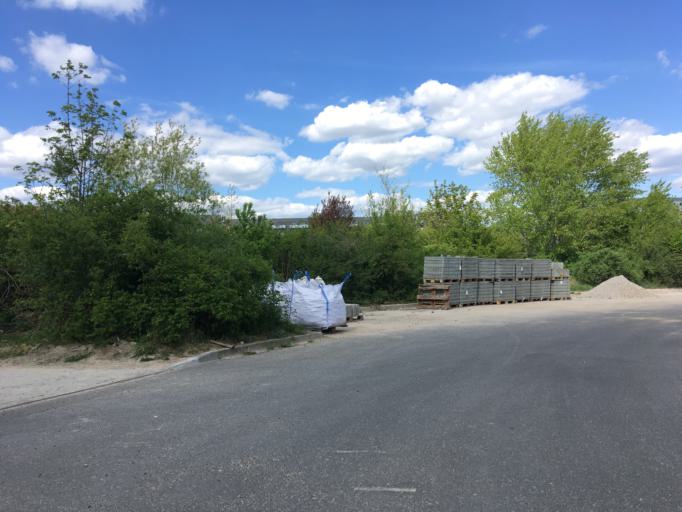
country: DE
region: Berlin
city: Hellersdorf
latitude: 52.5386
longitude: 13.6230
